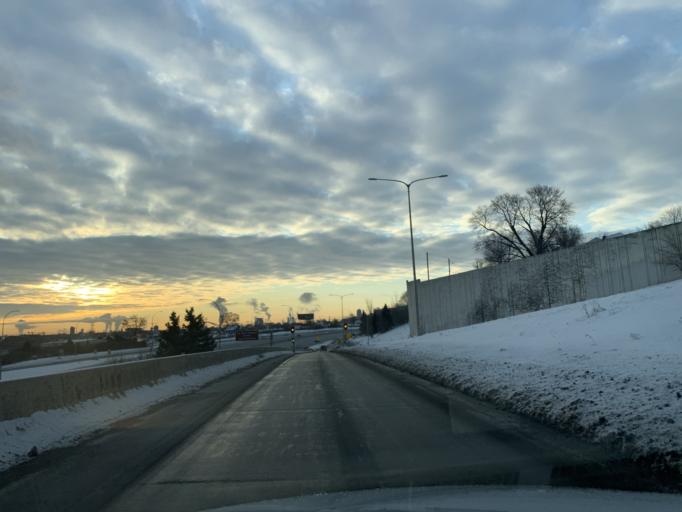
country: US
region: Minnesota
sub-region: Anoka County
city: Columbia Heights
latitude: 45.0226
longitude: -93.2846
